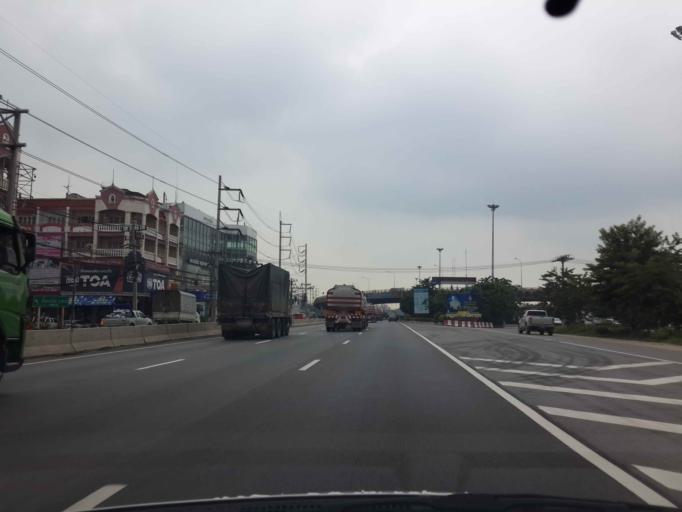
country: TH
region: Samut Sakhon
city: Samut Sakhon
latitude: 13.5882
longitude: 100.3258
